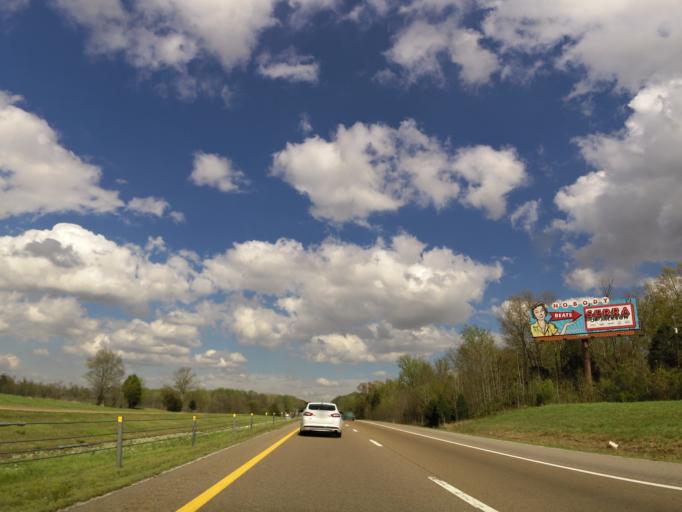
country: US
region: Tennessee
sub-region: Crockett County
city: Bells
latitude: 35.6168
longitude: -89.0007
